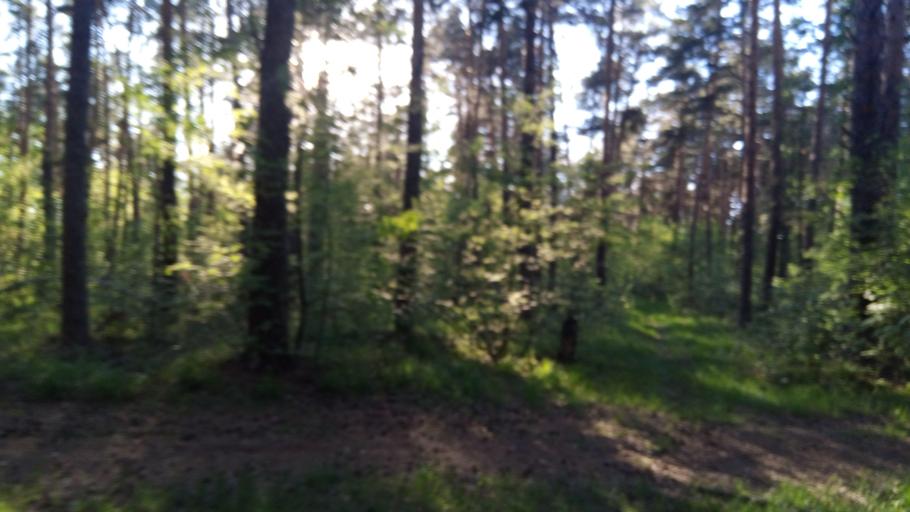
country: RU
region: Chelyabinsk
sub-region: Gorod Chelyabinsk
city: Chelyabinsk
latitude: 55.1357
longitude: 61.3303
